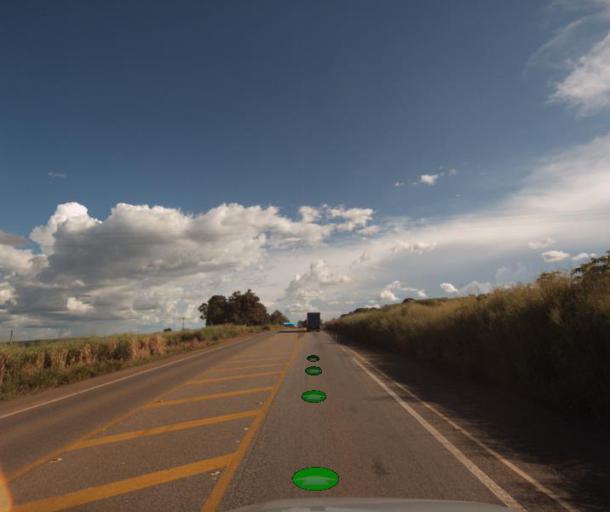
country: BR
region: Goias
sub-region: Porangatu
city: Porangatu
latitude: -13.1009
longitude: -49.1982
